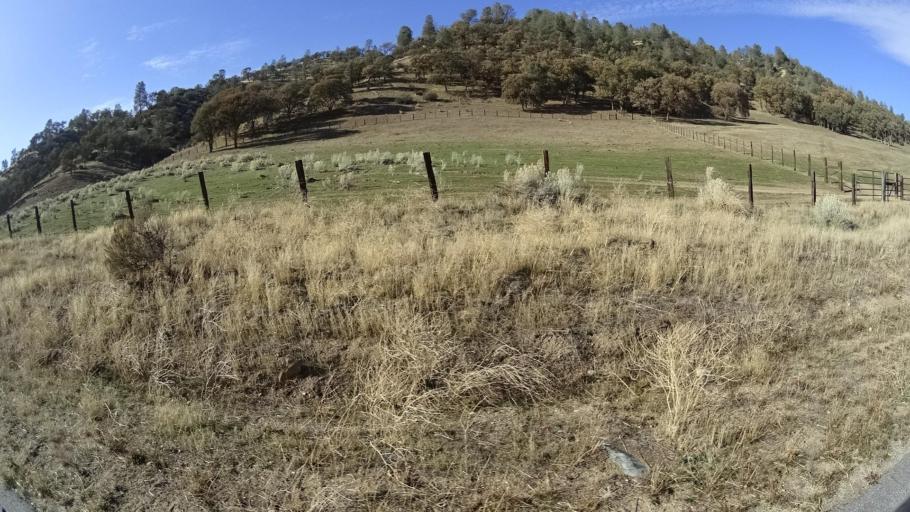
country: US
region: California
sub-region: Kern County
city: Bodfish
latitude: 35.3903
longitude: -118.5514
